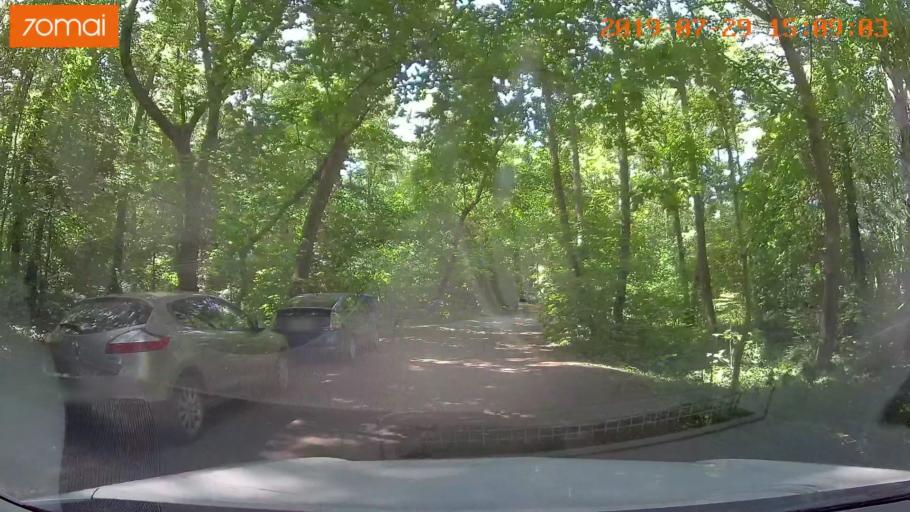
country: RU
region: Kaliningrad
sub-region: Gorod Kaliningrad
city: Baltiysk
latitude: 54.6809
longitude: 19.9162
